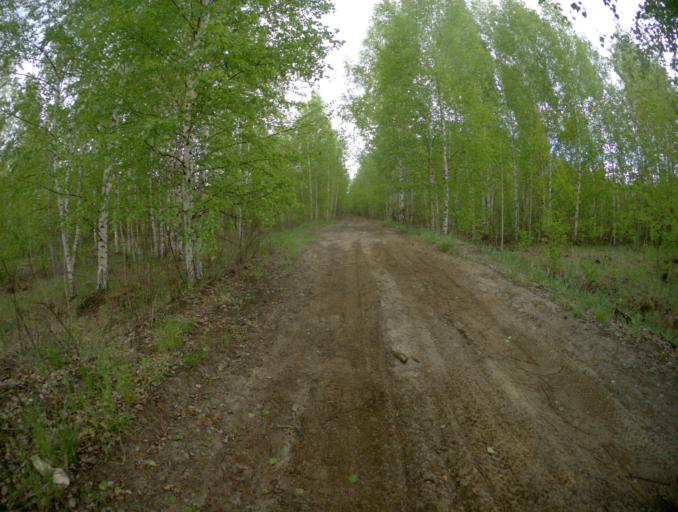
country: RU
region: Moskovskaya
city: Cherusti
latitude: 55.5905
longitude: 40.1249
